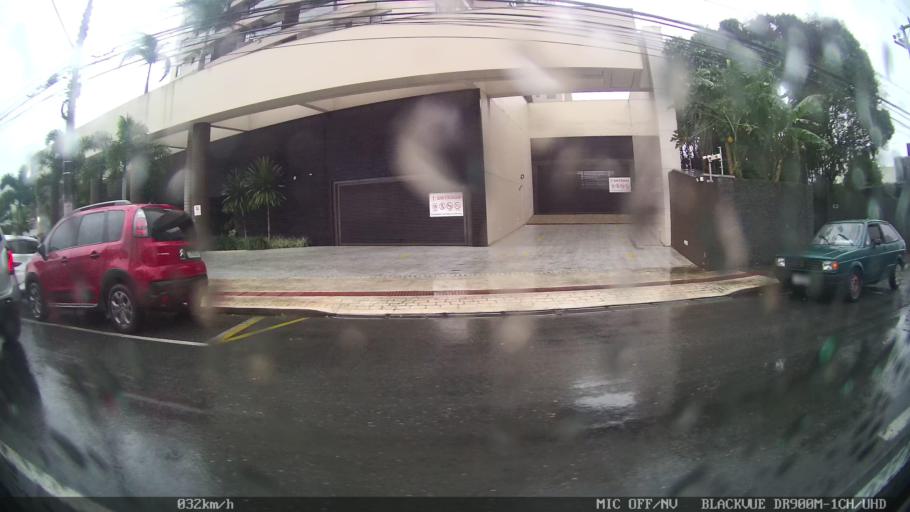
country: BR
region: Santa Catarina
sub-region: Itajai
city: Itajai
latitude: -26.9045
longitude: -48.6659
